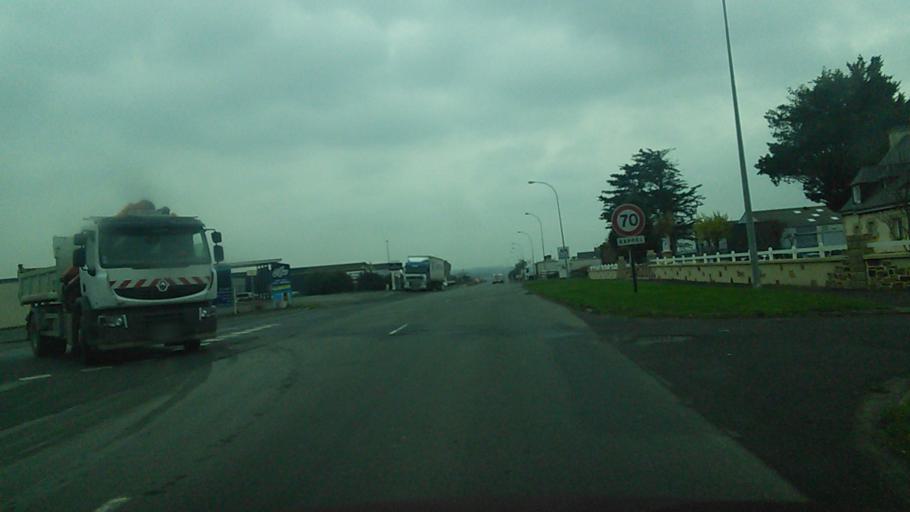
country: FR
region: Brittany
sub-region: Departement des Cotes-d'Armor
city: Yffiniac
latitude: 48.4852
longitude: -2.6527
